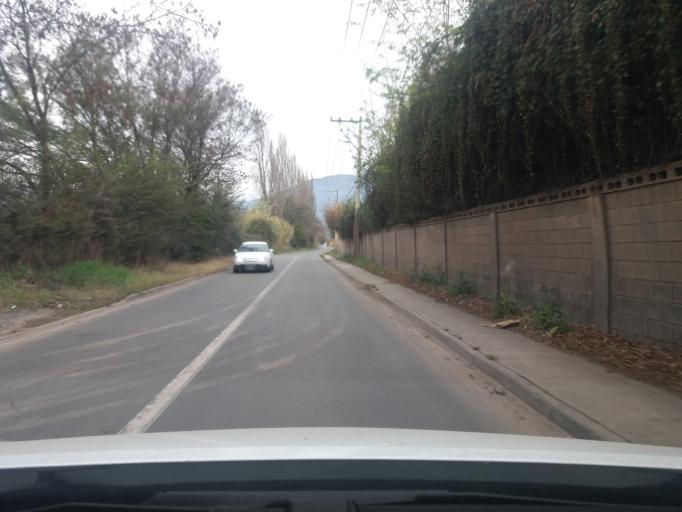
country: CL
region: Valparaiso
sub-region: Provincia de Los Andes
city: Los Andes
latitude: -32.8461
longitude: -70.6287
